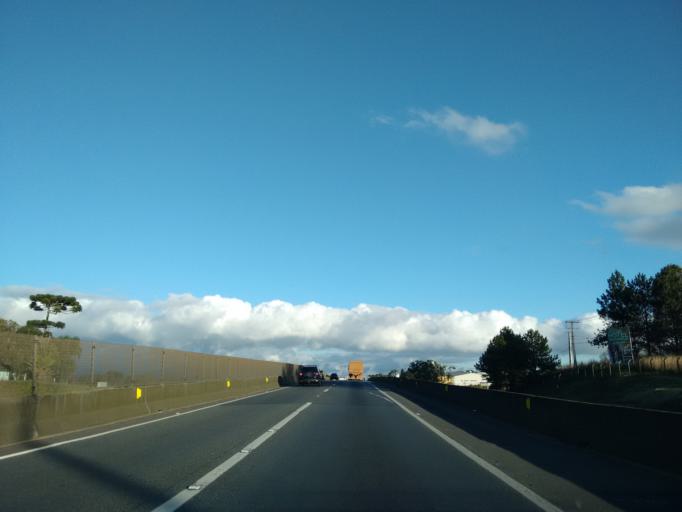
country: BR
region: Parana
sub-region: Sao Jose Dos Pinhais
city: Sao Jose dos Pinhais
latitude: -25.6645
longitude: -49.1539
